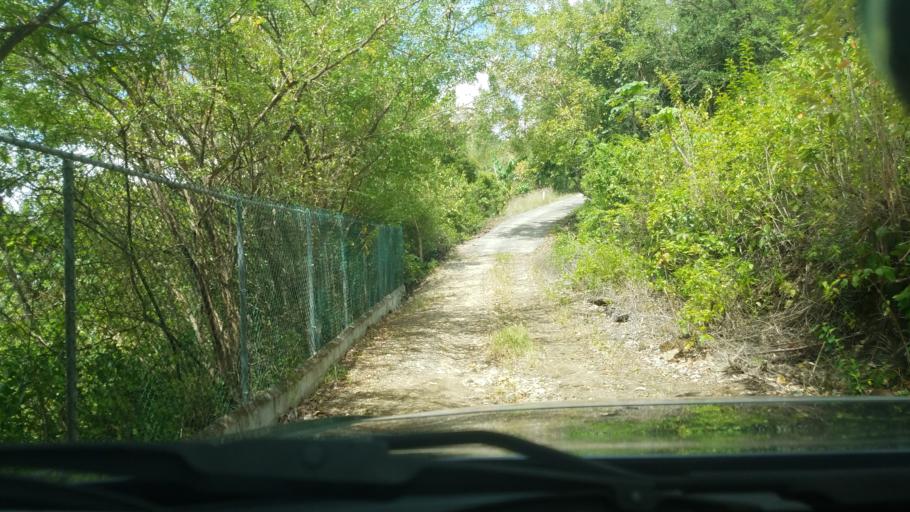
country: LC
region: Gros-Islet
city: Gros Islet
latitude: 14.0638
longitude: -60.9507
